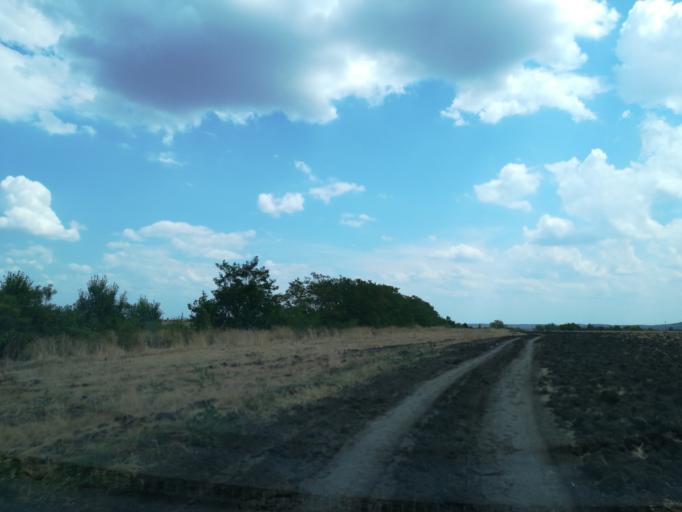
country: BG
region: Khaskovo
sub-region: Obshtina Mineralni Bani
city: Mineralni Bani
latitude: 41.9990
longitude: 25.1900
